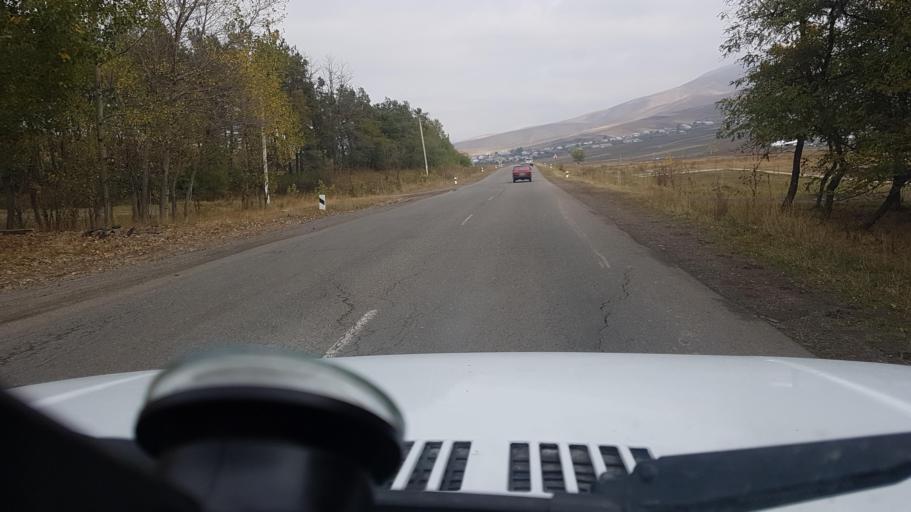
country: AZ
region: Gadabay Rayon
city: Ariqdam
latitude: 40.6224
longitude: 45.8144
